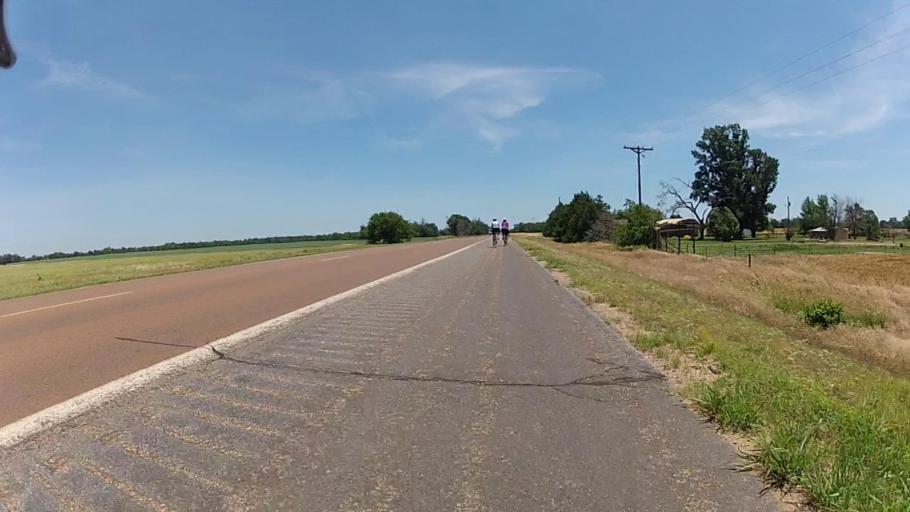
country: US
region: Kansas
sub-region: Barber County
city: Medicine Lodge
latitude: 37.2534
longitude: -98.3412
